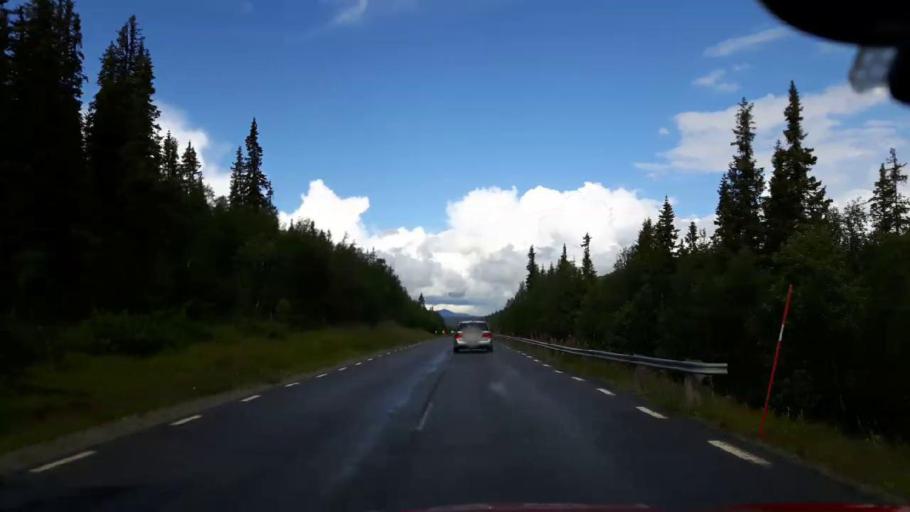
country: SE
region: Vaesterbotten
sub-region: Vilhelmina Kommun
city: Sjoberg
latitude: 65.0276
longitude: 15.1457
